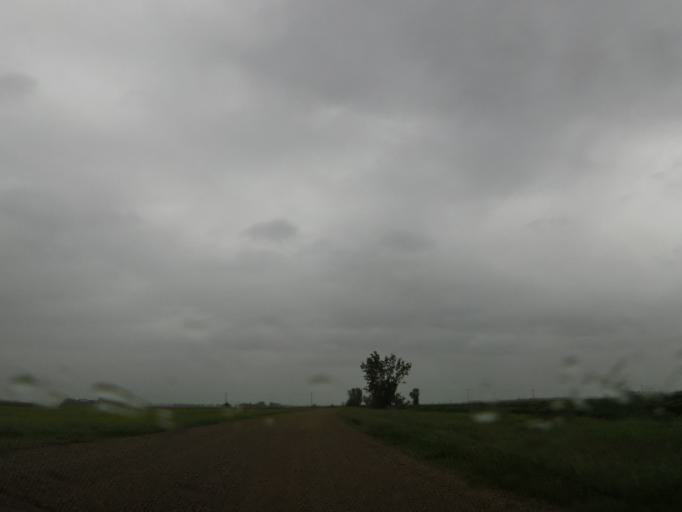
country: US
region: North Dakota
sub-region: Walsh County
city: Grafton
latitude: 48.4378
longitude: -97.4054
